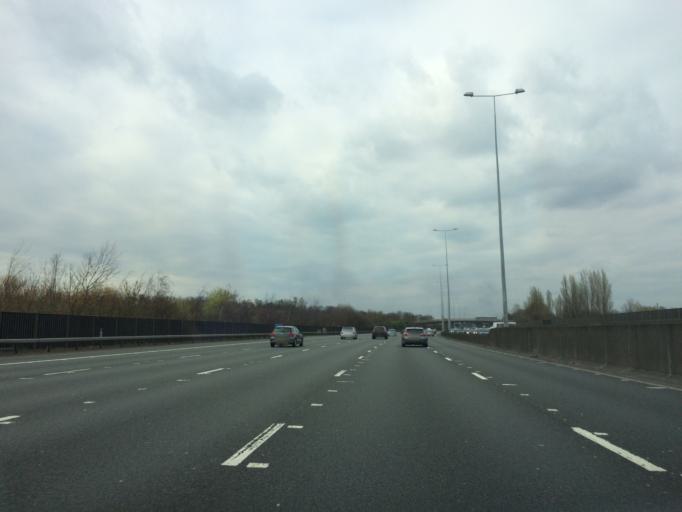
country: GB
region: England
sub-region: Surrey
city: Egham
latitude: 51.4101
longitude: -0.5411
